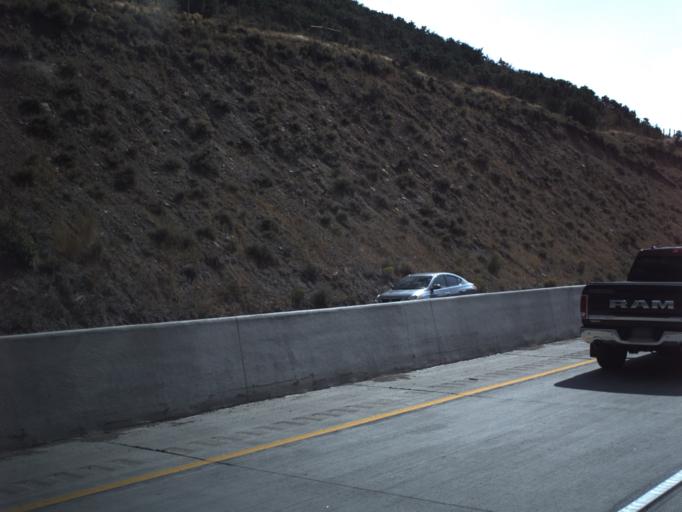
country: US
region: Utah
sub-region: Summit County
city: Coalville
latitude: 40.7999
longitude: -111.4441
